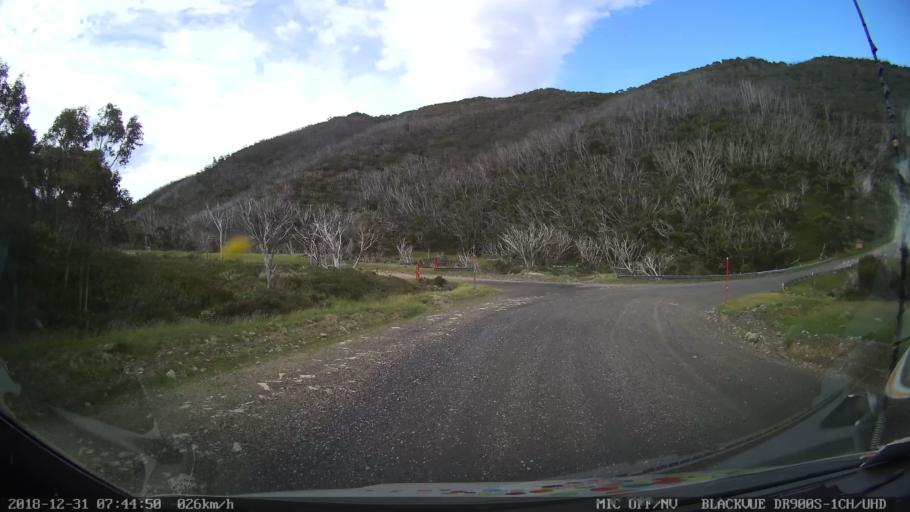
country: AU
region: New South Wales
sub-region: Snowy River
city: Jindabyne
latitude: -36.3659
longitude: 148.4051
